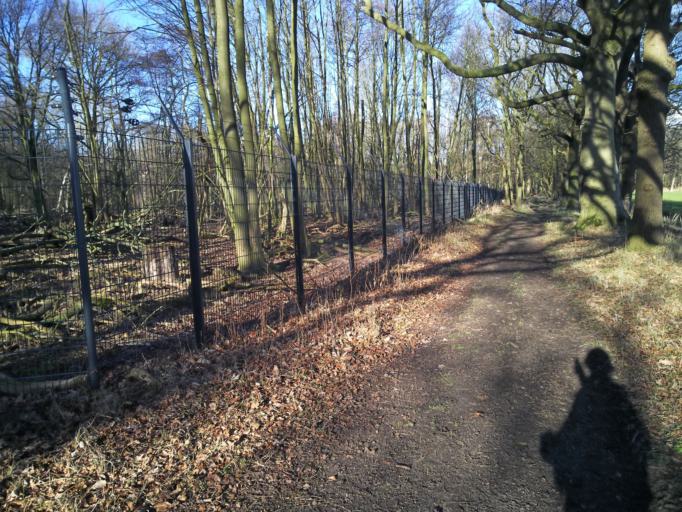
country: NL
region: North Holland
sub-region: Gemeente Bloemendaal
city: Bennebroek
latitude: 52.3338
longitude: 4.5702
